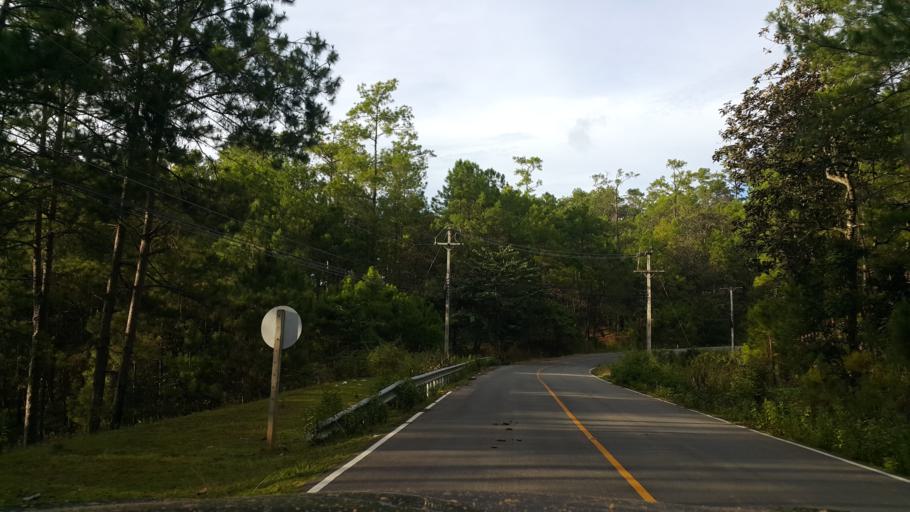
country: TH
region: Chiang Mai
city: Chaem Luang
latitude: 19.0866
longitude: 98.3385
